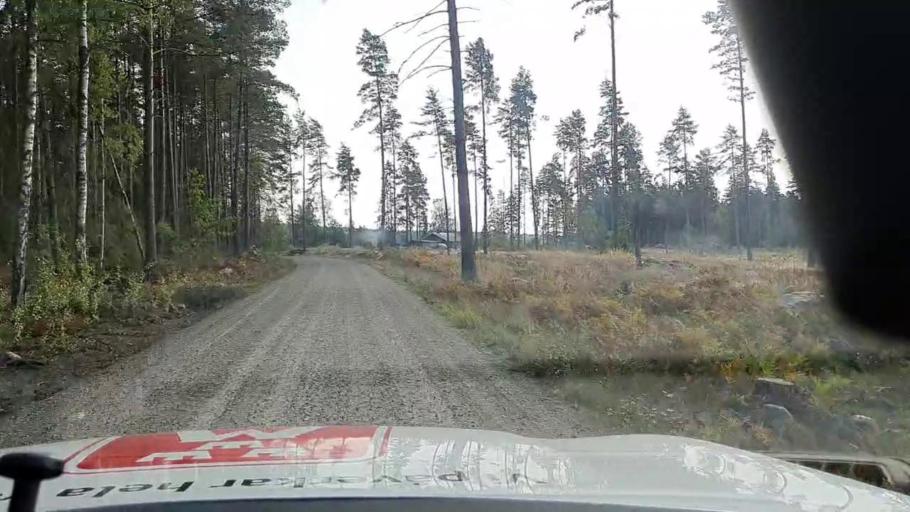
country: SE
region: Vaestmanland
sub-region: Kungsors Kommun
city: Kungsoer
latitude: 59.3568
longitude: 16.1527
